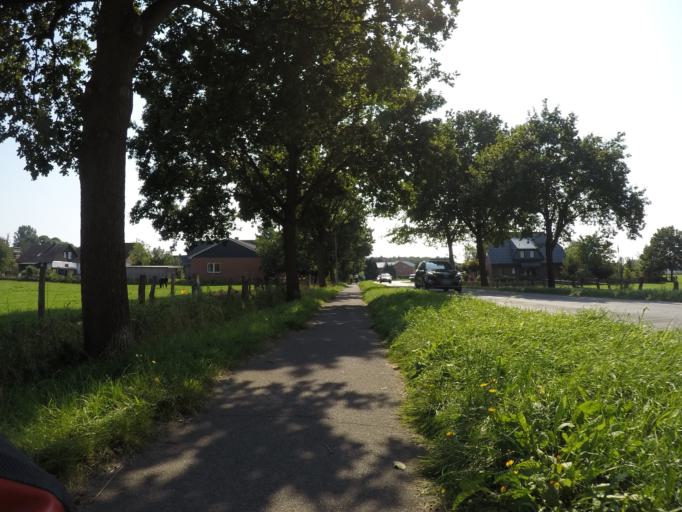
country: DE
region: Schleswig-Holstein
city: Stuvenborn
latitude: 53.8497
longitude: 10.1203
